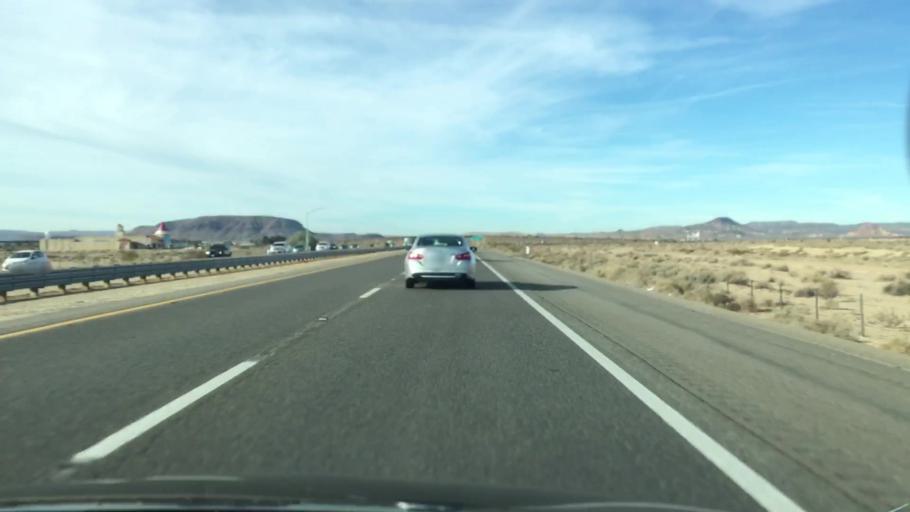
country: US
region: California
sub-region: San Bernardino County
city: Barstow
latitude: 34.9113
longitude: -116.8255
